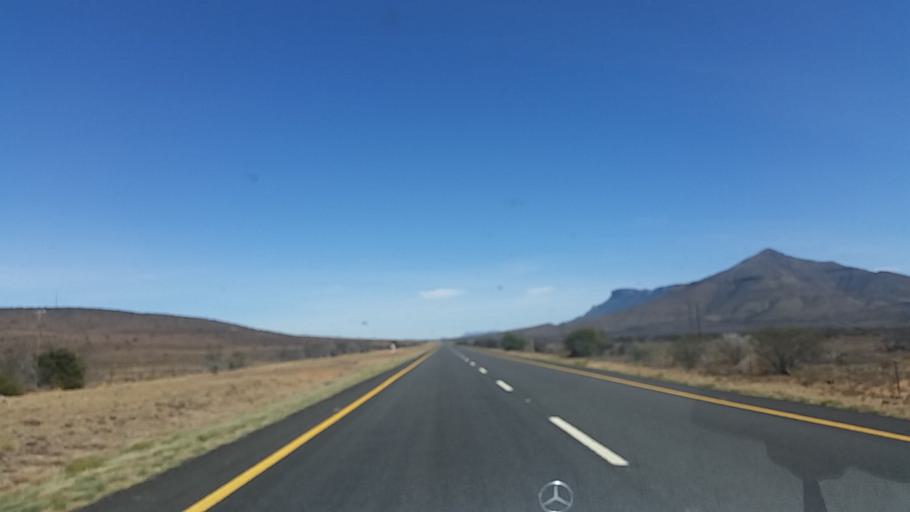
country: ZA
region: Eastern Cape
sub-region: Cacadu District Municipality
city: Graaff-Reinet
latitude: -32.3519
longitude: 24.3174
